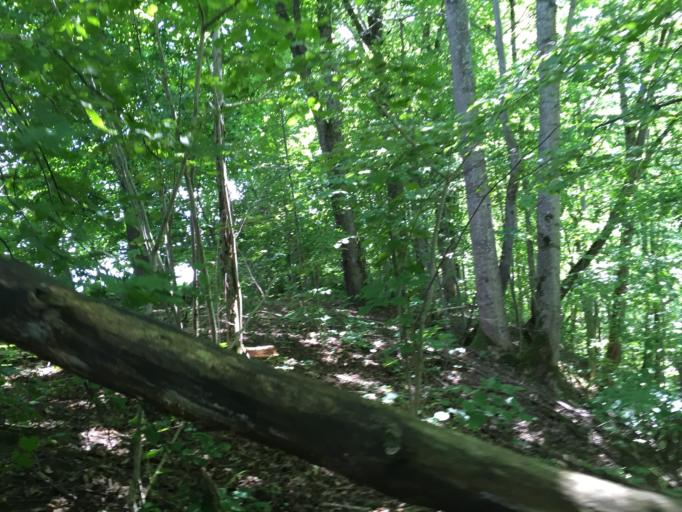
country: LV
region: Sigulda
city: Sigulda
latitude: 57.1860
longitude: 24.9339
